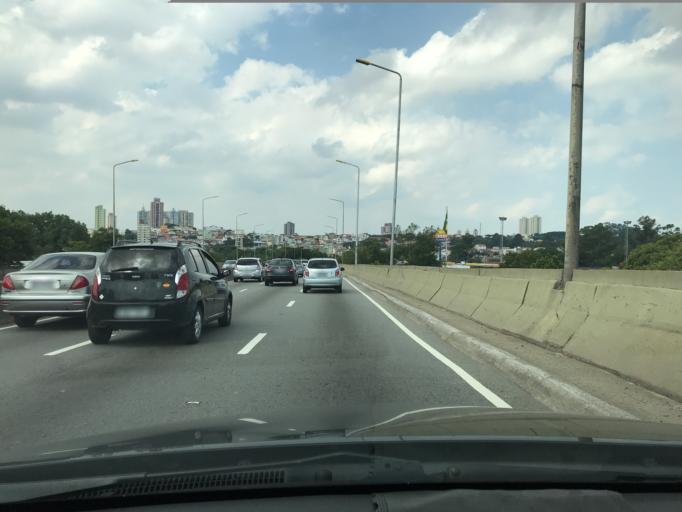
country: BR
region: Sao Paulo
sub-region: Santo Andre
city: Santo Andre
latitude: -23.6527
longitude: -46.5277
